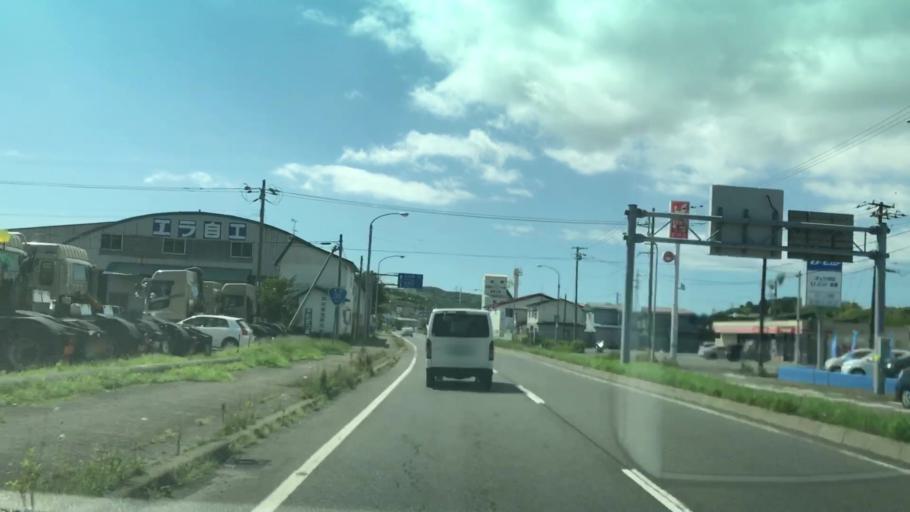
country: JP
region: Hokkaido
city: Muroran
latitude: 42.3401
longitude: 141.0286
